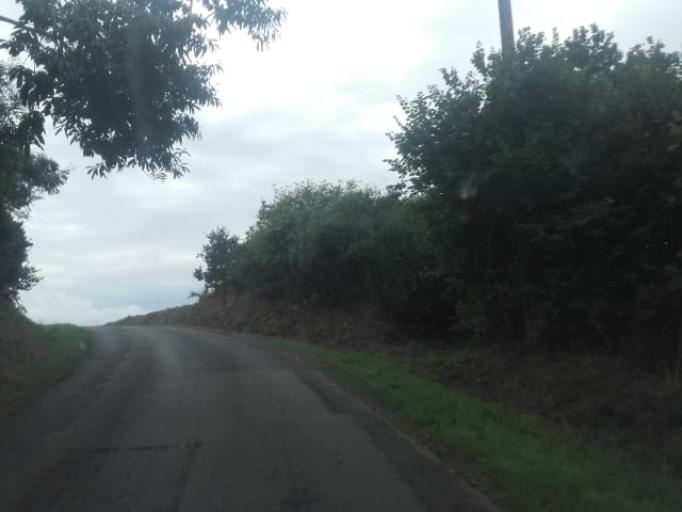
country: FR
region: Brittany
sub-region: Departement des Cotes-d'Armor
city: Pordic
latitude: 48.5596
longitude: -2.8440
